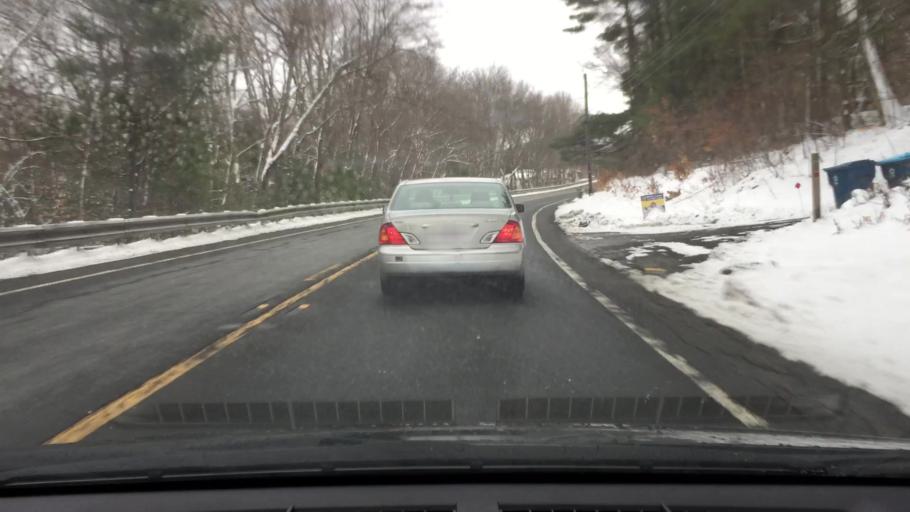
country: US
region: Massachusetts
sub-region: Hampshire County
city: Pelham
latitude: 42.3426
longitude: -72.4028
